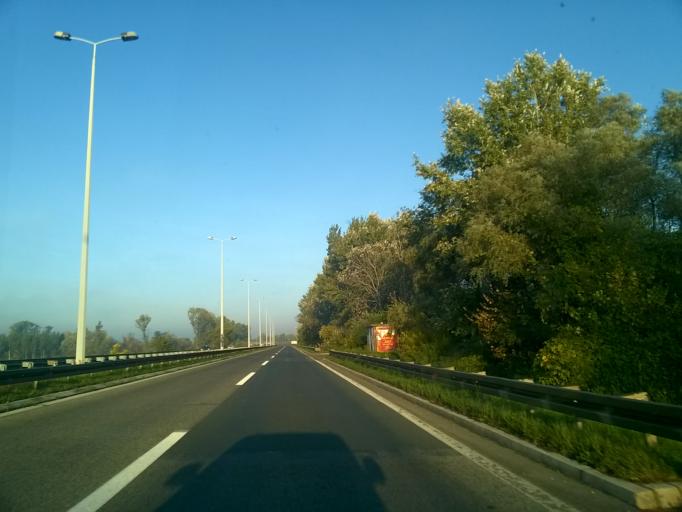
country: RS
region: Autonomna Pokrajina Vojvodina
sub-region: Juznobanatski Okrug
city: Pancevo
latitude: 44.8612
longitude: 20.5897
